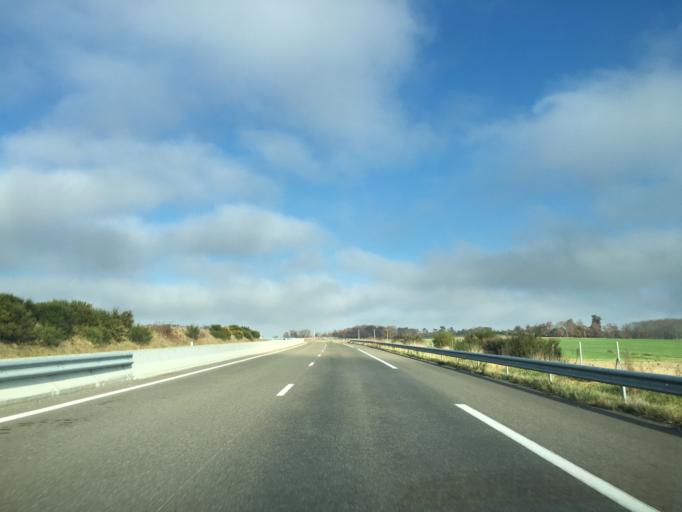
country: FR
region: Midi-Pyrenees
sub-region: Departement du Gers
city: Barcelonne-du-Gers
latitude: 43.7661
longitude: -0.2735
